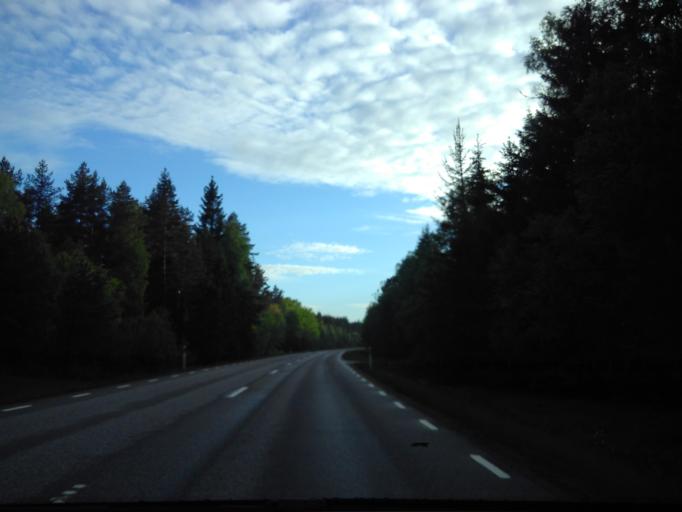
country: SE
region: Vaestra Goetaland
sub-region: Herrljunga Kommun
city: Herrljunga
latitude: 58.0613
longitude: 13.0721
